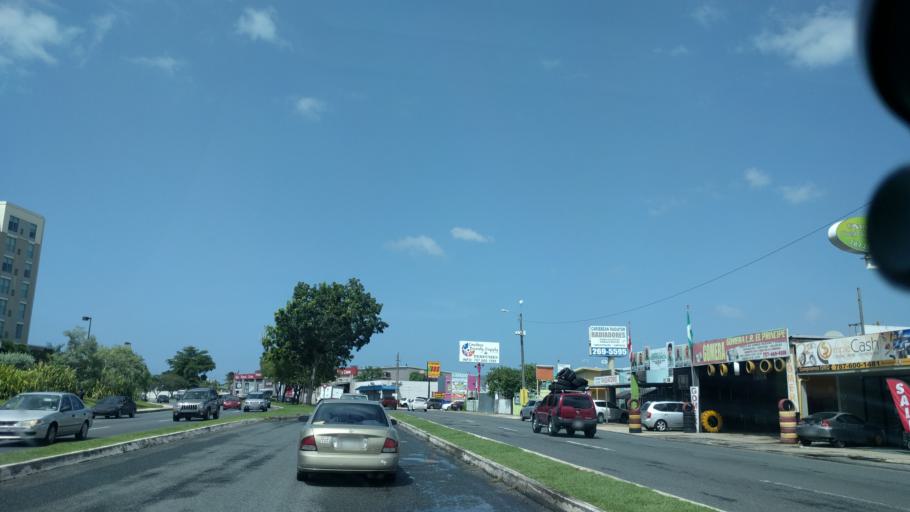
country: PR
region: Bayamon
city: Bayamon
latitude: 18.4075
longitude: -66.1597
